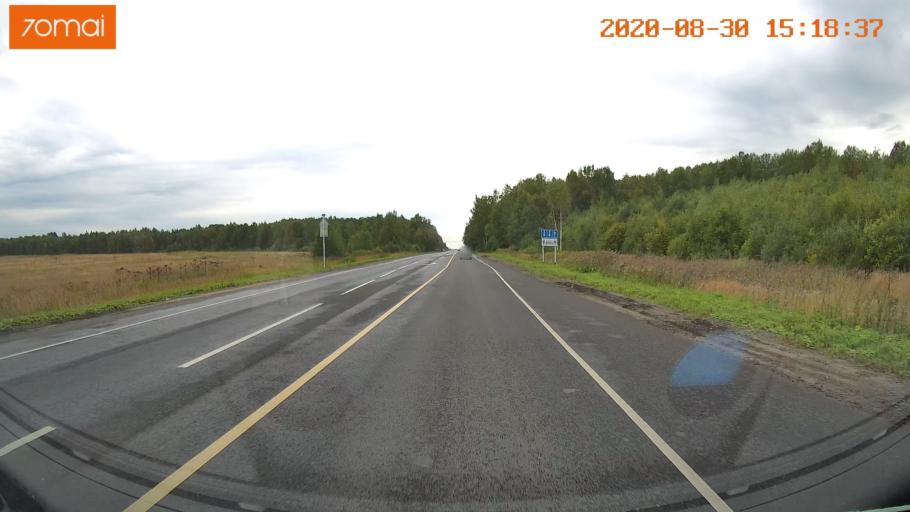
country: RU
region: Ivanovo
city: Rodniki
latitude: 57.1211
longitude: 41.7916
